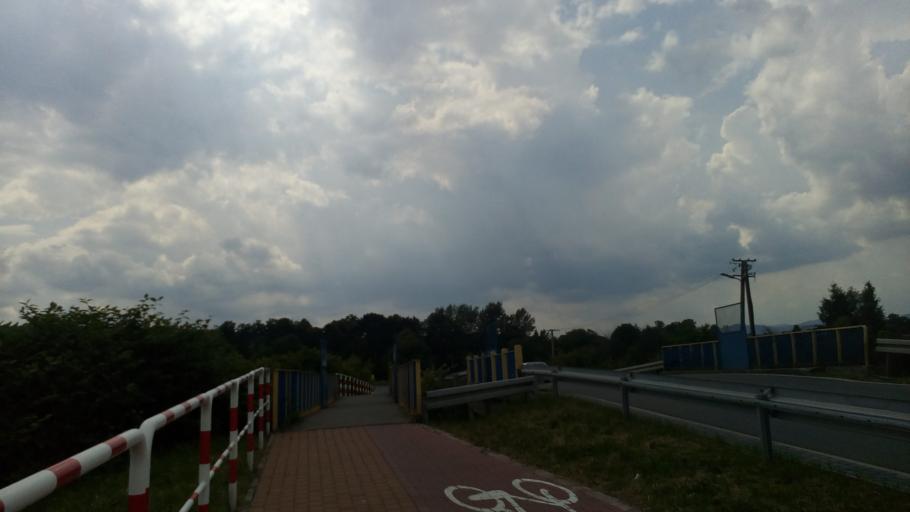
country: PL
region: Lesser Poland Voivodeship
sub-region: Powiat nowosadecki
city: Stary Sacz
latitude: 49.5657
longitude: 20.6429
